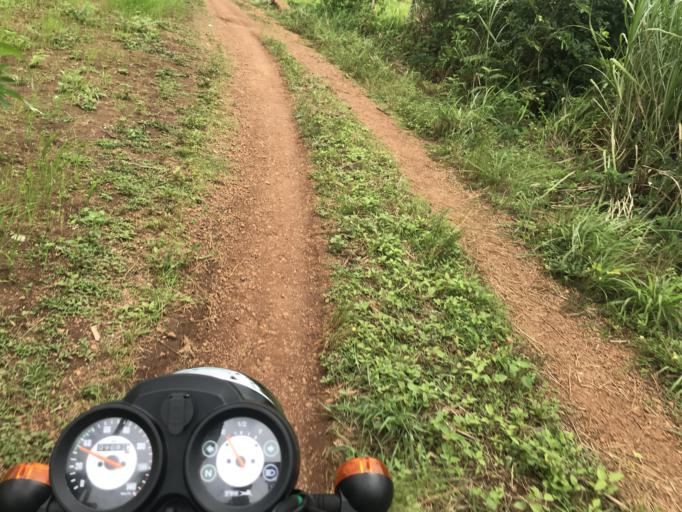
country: SL
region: Eastern Province
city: Buedu
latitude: 8.4771
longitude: -10.3183
